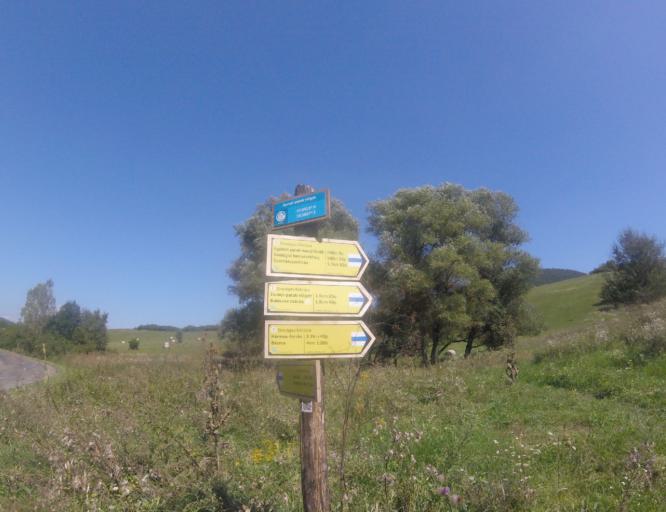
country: HU
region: Nograd
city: Bujak
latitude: 47.9418
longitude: 19.5887
